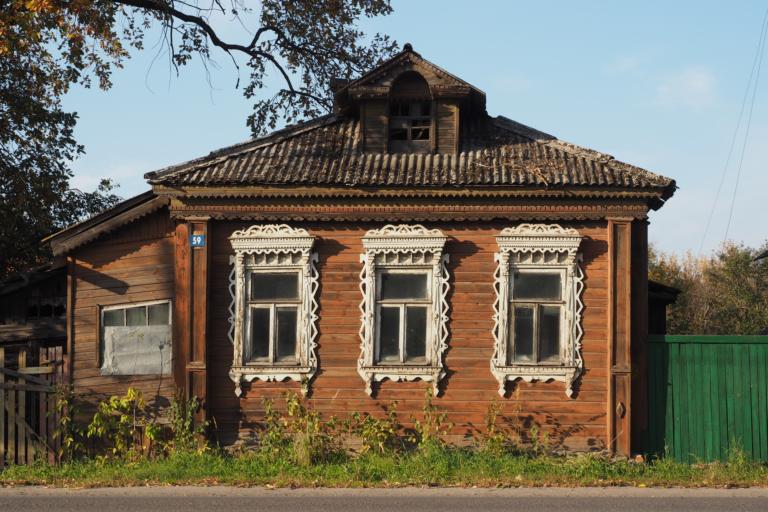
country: RU
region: Moskovskaya
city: Kurovskoye
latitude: 55.5782
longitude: 38.9085
